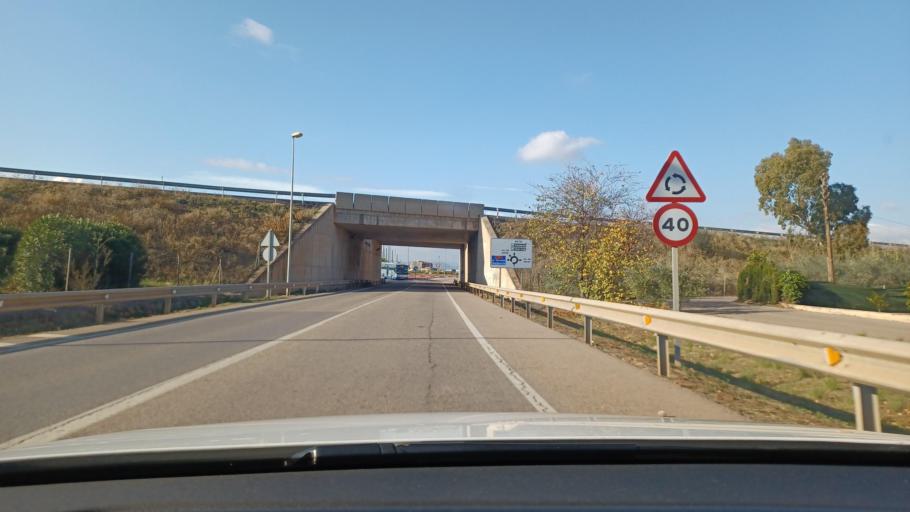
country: ES
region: Valencia
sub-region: Provincia de Castello
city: Betxi
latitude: 39.9260
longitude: -0.1903
